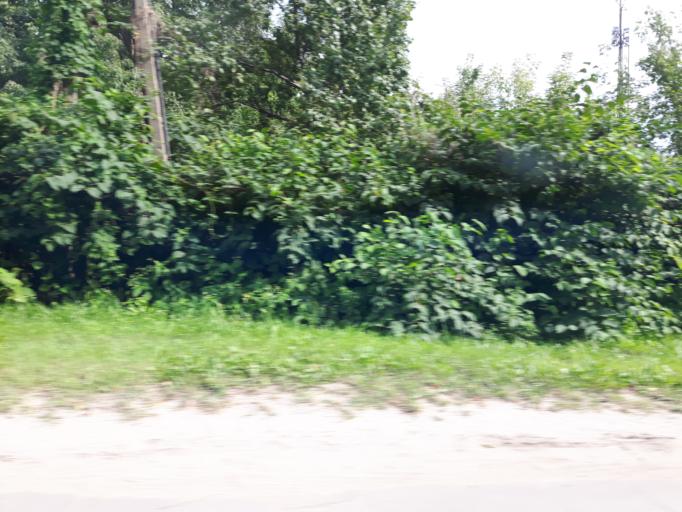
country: PL
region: Masovian Voivodeship
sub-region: Warszawa
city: Praga Poludnie
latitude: 52.2713
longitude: 21.0817
